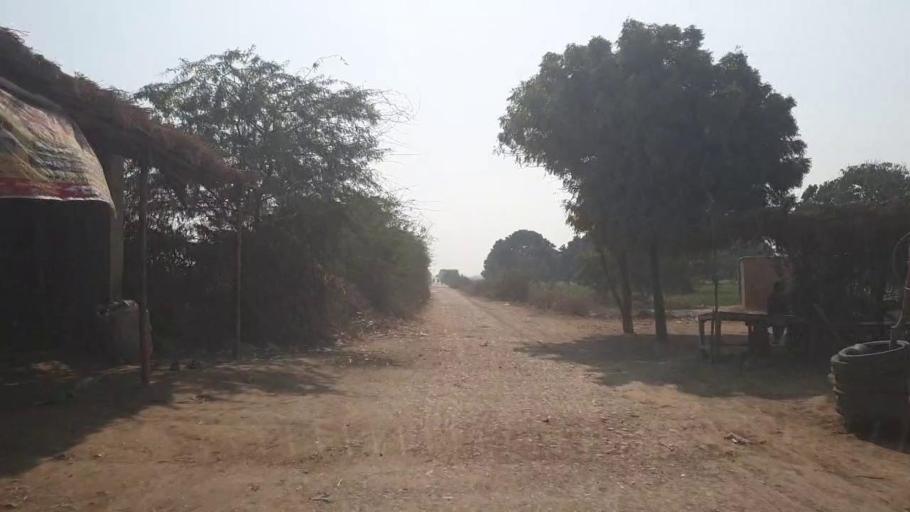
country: PK
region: Sindh
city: Tando Allahyar
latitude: 25.4822
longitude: 68.8020
